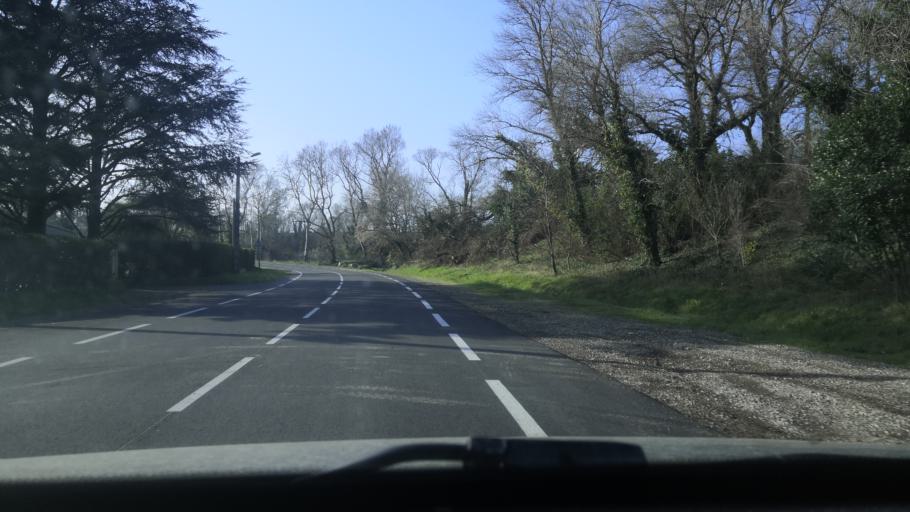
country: FR
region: Rhone-Alpes
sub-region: Departement de la Drome
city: Ancone
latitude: 44.5578
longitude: 4.7183
